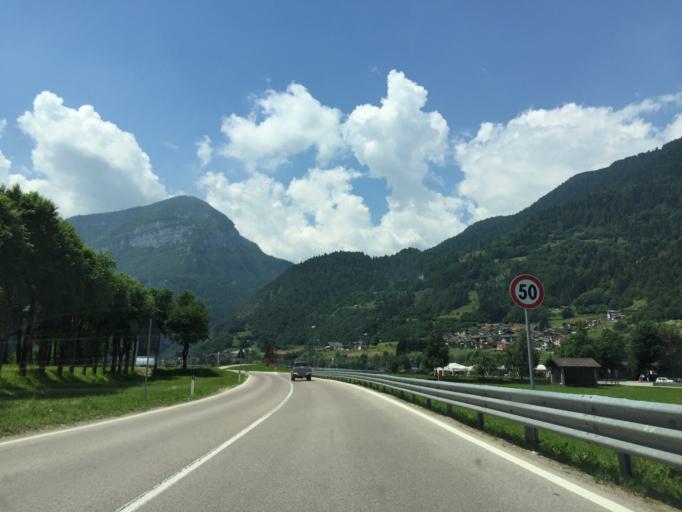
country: IT
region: Trentino-Alto Adige
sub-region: Provincia di Trento
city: Imer
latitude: 46.1476
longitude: 11.7987
